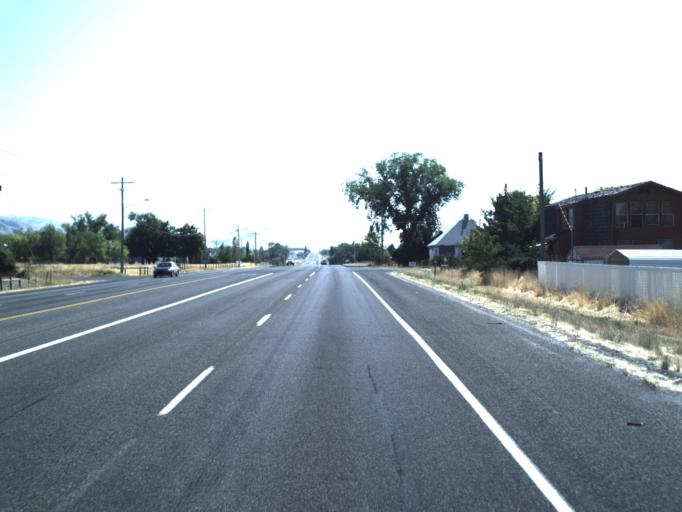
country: US
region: Utah
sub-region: Cache County
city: Richmond
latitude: 41.9444
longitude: -111.8138
